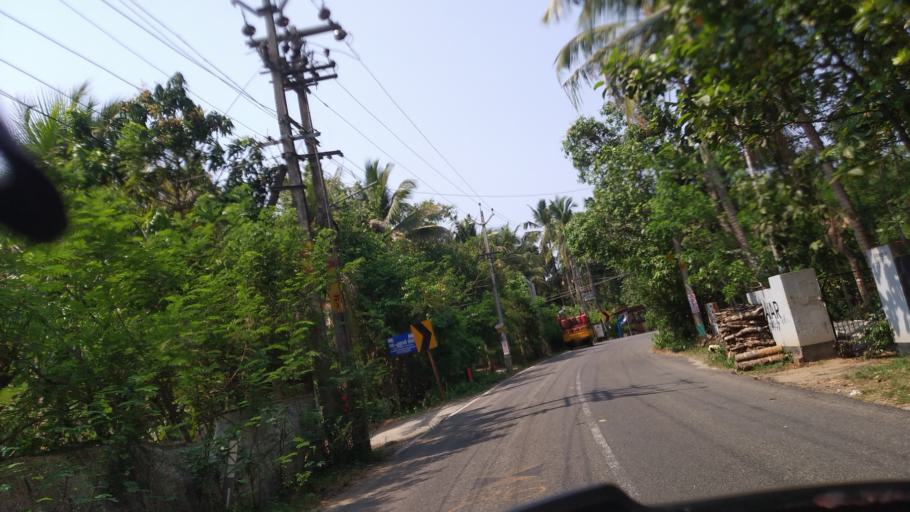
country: IN
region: Kerala
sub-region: Thrissur District
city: Irinjalakuda
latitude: 10.2964
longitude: 76.1323
